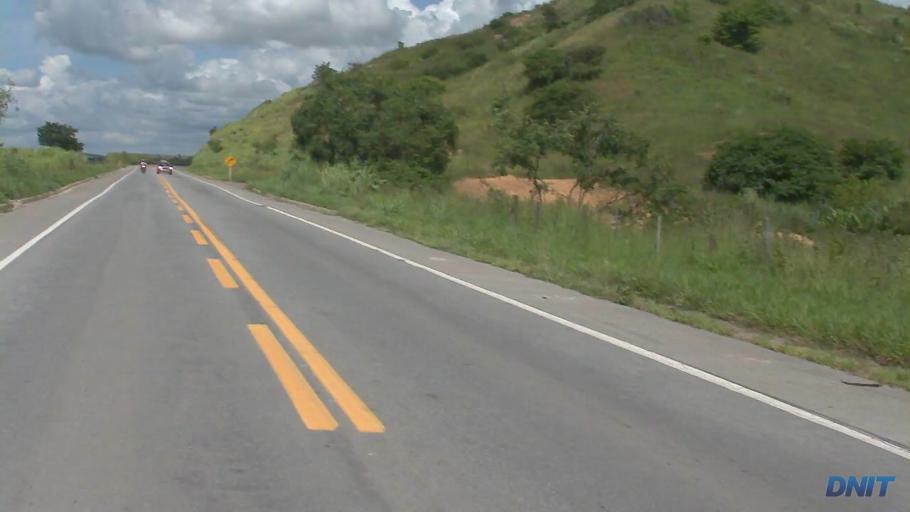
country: BR
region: Minas Gerais
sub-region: Governador Valadares
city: Governador Valadares
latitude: -18.9719
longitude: -42.0944
